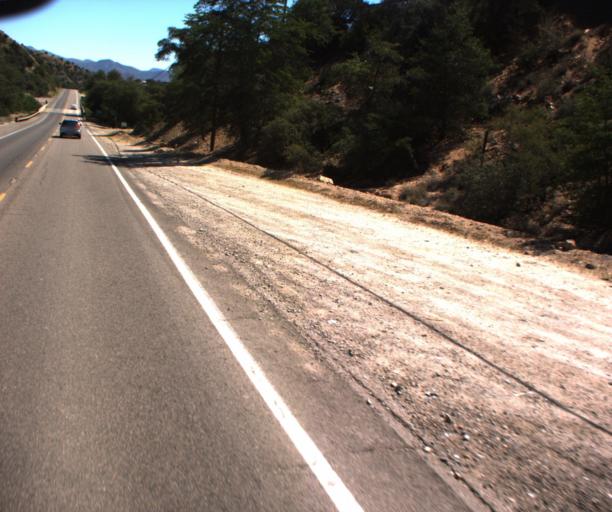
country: US
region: Arizona
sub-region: Gila County
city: Miami
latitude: 33.3839
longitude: -110.8922
